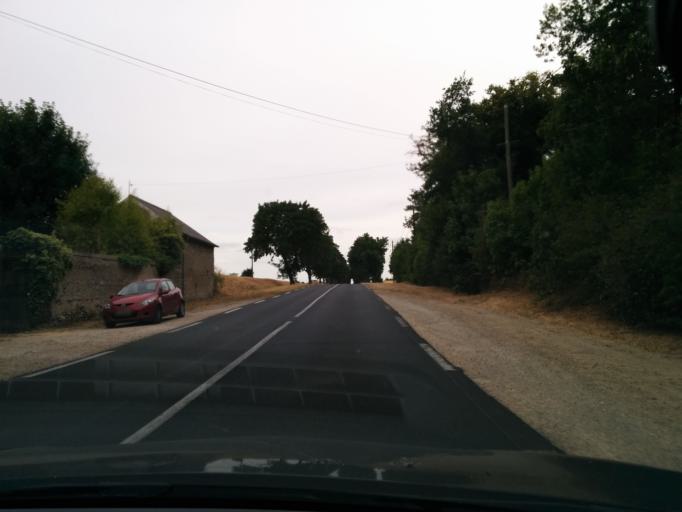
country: FR
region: Ile-de-France
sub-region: Departement de l'Essonne
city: Pussay
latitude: 48.3594
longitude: 1.9836
